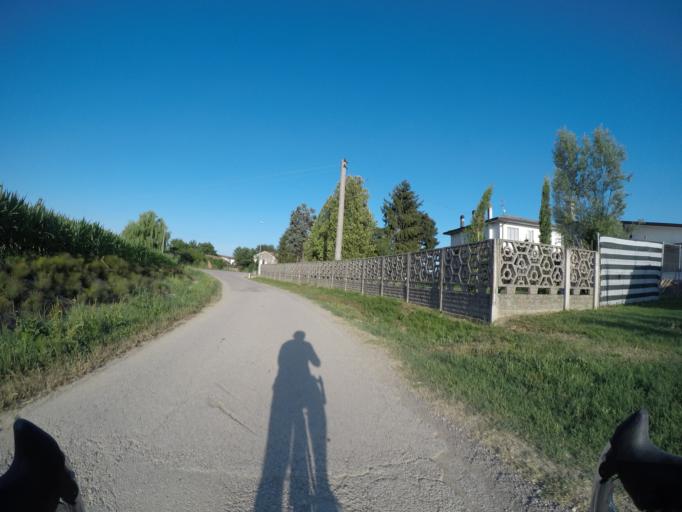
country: IT
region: Veneto
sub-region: Provincia di Rovigo
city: Villamarzana
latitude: 45.0251
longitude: 11.6752
